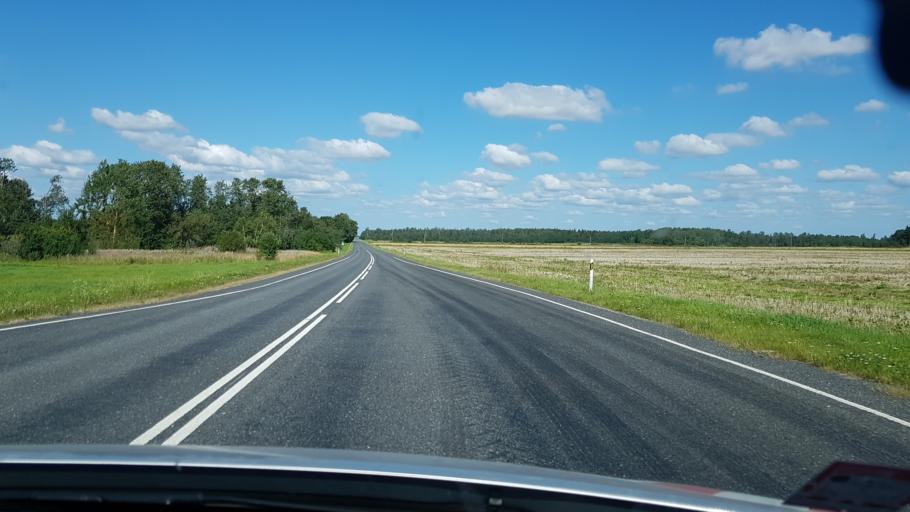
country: EE
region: Jaervamaa
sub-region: Jaerva-Jaani vald
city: Jarva-Jaani
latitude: 59.1166
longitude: 25.7929
